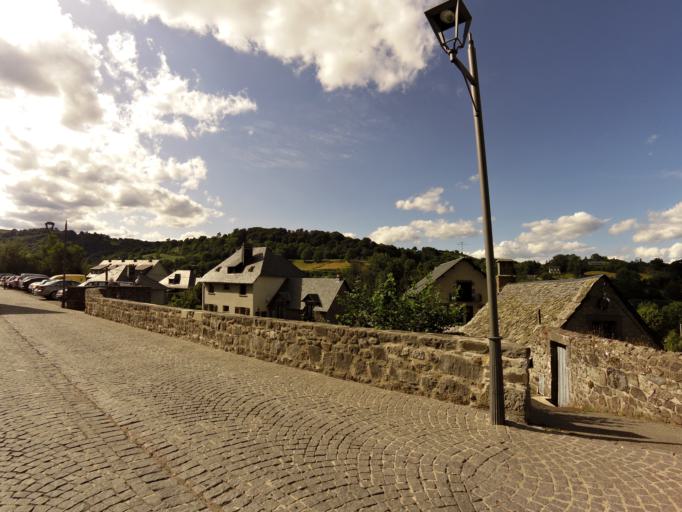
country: FR
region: Auvergne
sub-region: Departement du Puy-de-Dome
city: Mont-Dore
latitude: 45.5129
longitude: 2.9337
